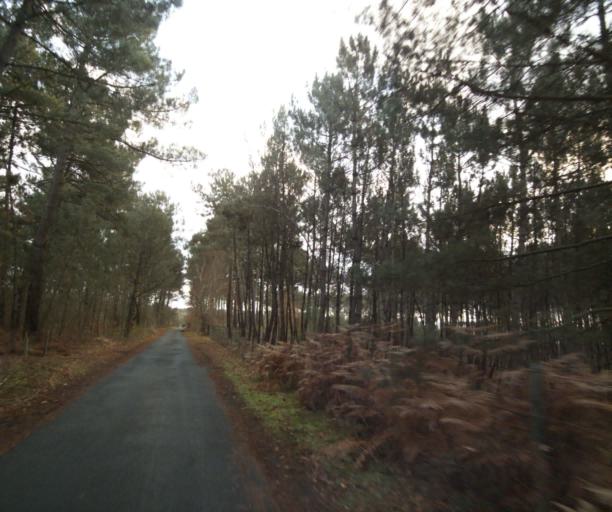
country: FR
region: Pays de la Loire
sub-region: Departement de la Sarthe
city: Ruaudin
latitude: 47.9629
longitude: 0.2276
